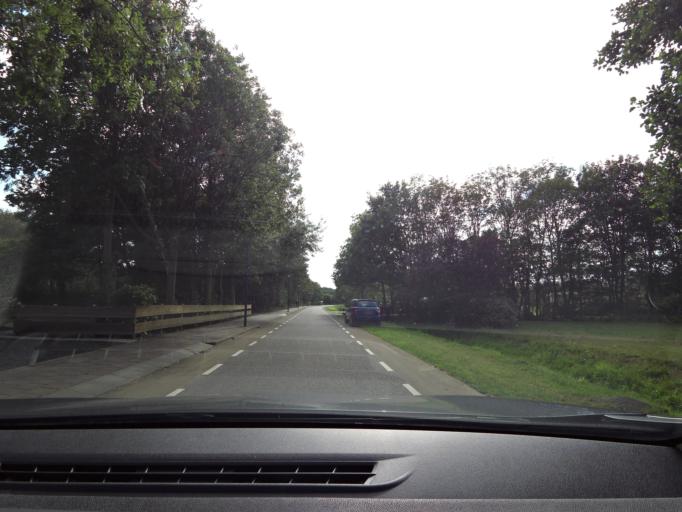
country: NL
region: South Holland
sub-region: Gemeente Goeree-Overflakkee
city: Ouddorp
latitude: 51.8241
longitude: 3.9259
